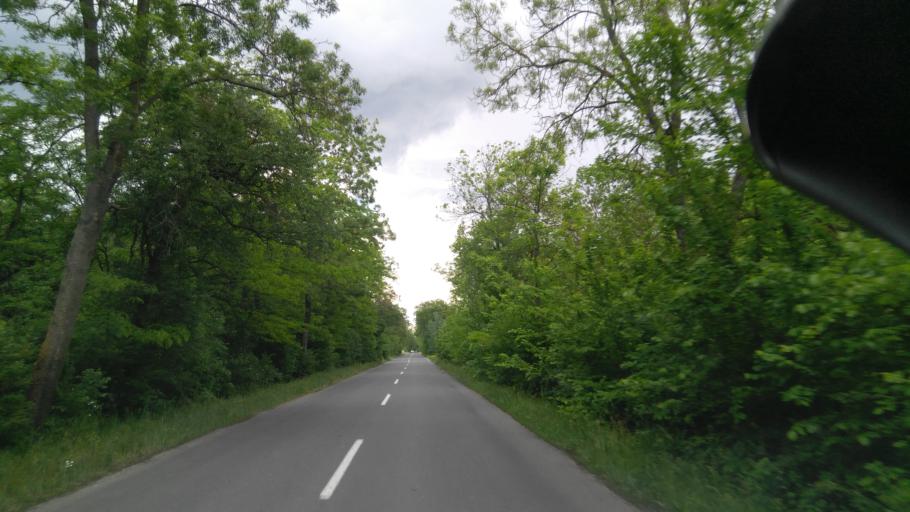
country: HU
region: Bekes
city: Bucsa
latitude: 47.1728
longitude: 21.0677
